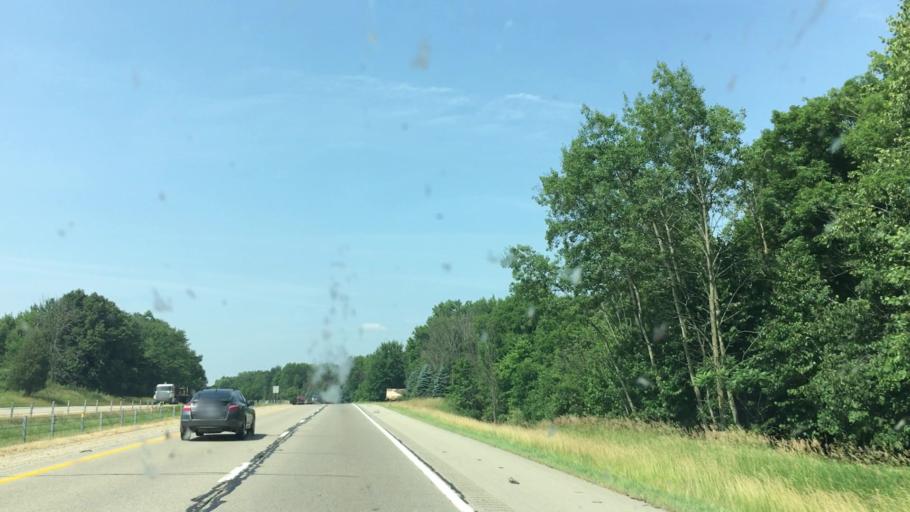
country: US
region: Michigan
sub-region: Allegan County
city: Wayland
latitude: 42.6022
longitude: -85.6605
